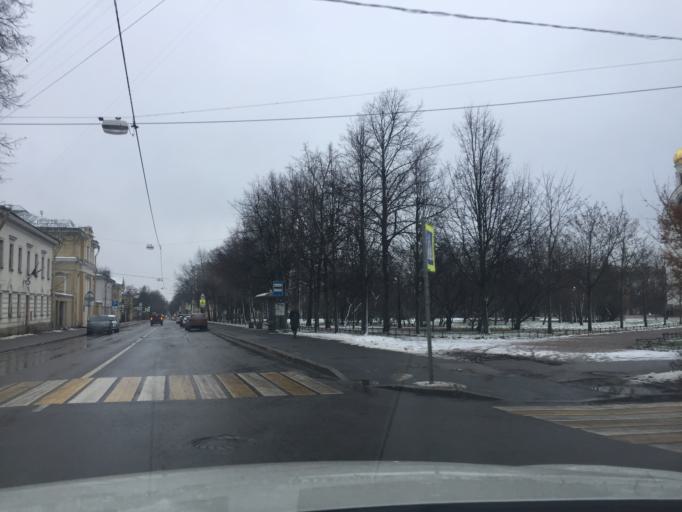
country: RU
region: St.-Petersburg
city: Pushkin
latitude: 59.7203
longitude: 30.4045
